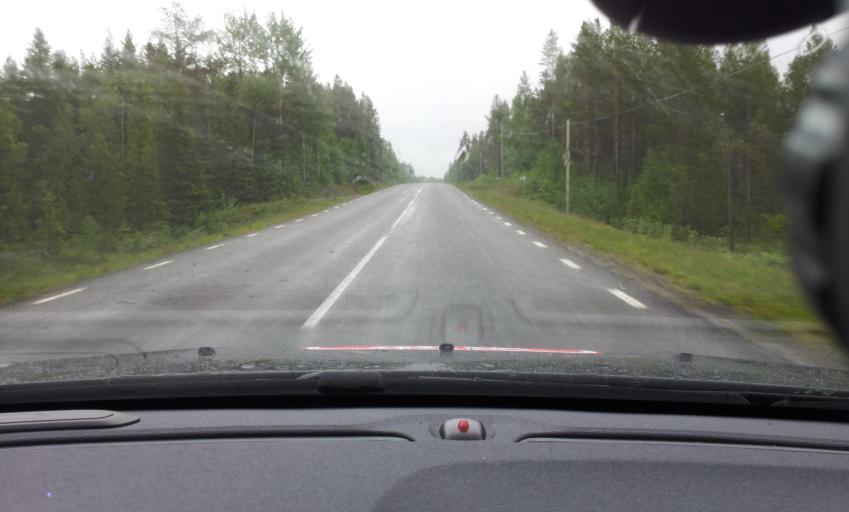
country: SE
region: Jaemtland
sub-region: Are Kommun
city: Are
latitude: 63.2216
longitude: 13.1067
